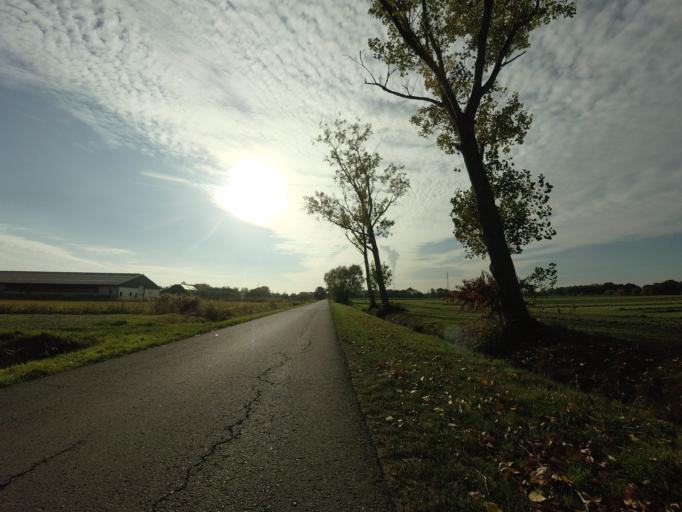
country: BE
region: Flanders
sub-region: Provincie Antwerpen
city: Stabroek
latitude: 51.3477
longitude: 4.3578
